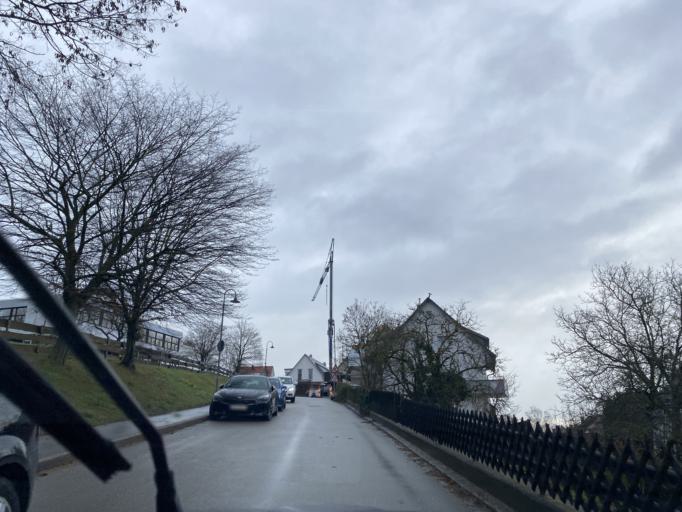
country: DE
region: Baden-Wuerttemberg
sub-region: Regierungsbezirk Stuttgart
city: Weissach
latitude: 48.8495
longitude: 8.9283
